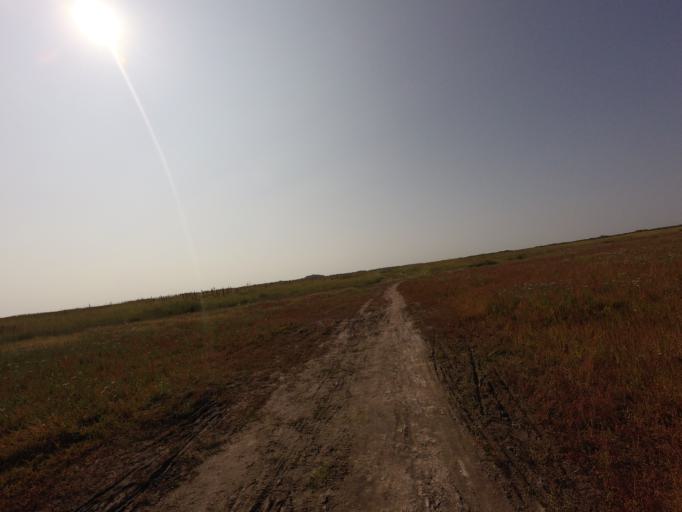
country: NL
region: Friesland
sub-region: Gemeente Schiermonnikoog
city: Schiermonnikoog
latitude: 53.4906
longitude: 6.2378
